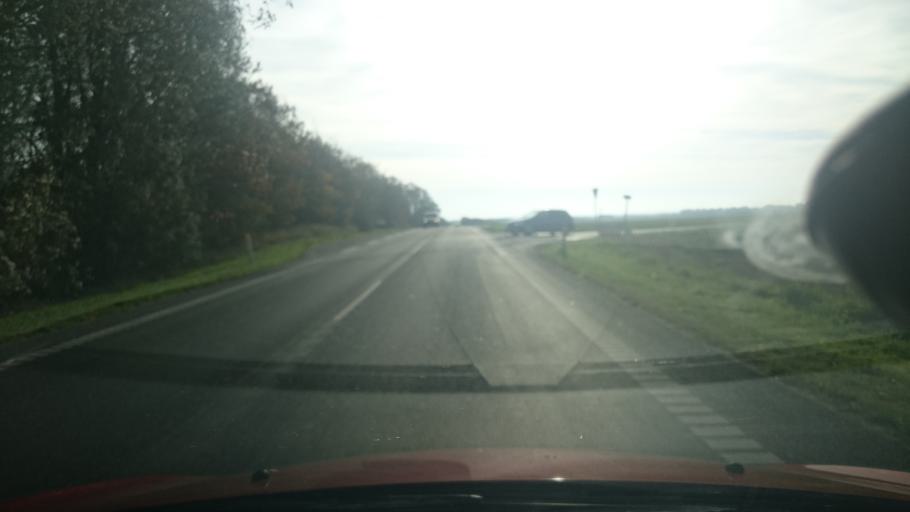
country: DK
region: Central Jutland
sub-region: Randers Kommune
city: Assentoft
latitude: 56.4354
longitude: 10.1866
